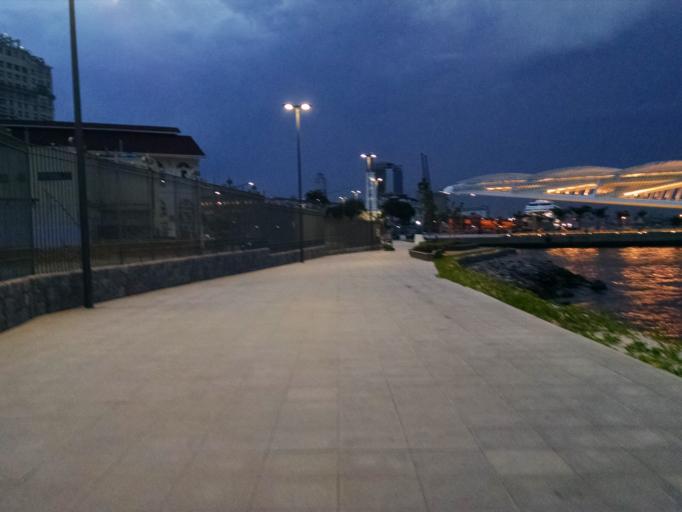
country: BR
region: Rio de Janeiro
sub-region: Rio De Janeiro
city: Rio de Janeiro
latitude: -22.8958
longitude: -43.1779
